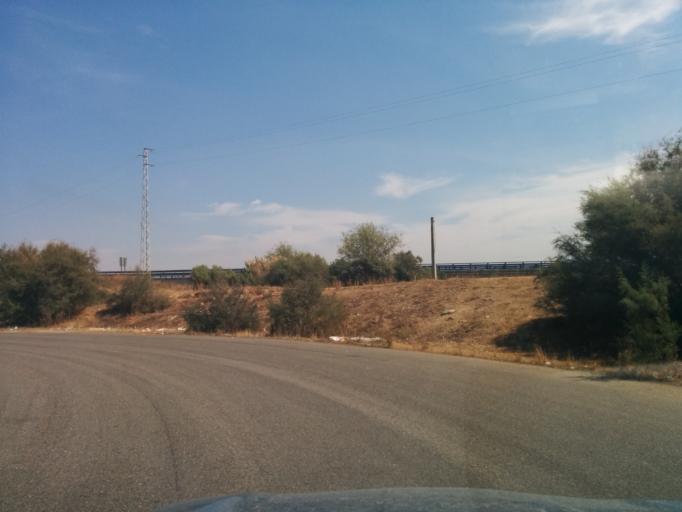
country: ES
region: Andalusia
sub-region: Provincia de Sevilla
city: Gelves
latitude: 37.3215
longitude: -5.9851
